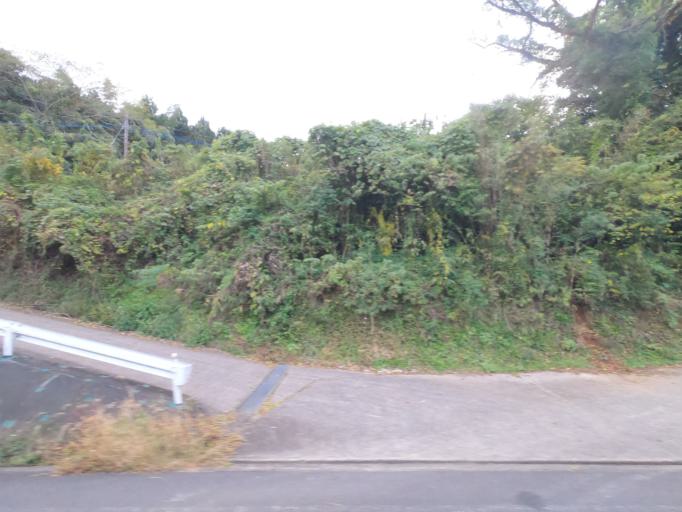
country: JP
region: Kumamoto
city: Minamata
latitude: 32.2627
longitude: 130.5079
